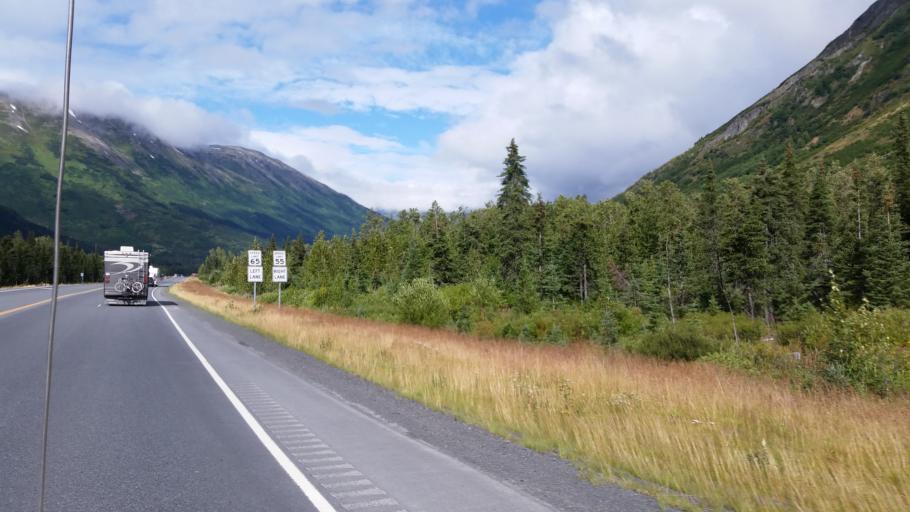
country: US
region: Alaska
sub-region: Anchorage Municipality
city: Girdwood
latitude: 60.7276
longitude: -149.3032
